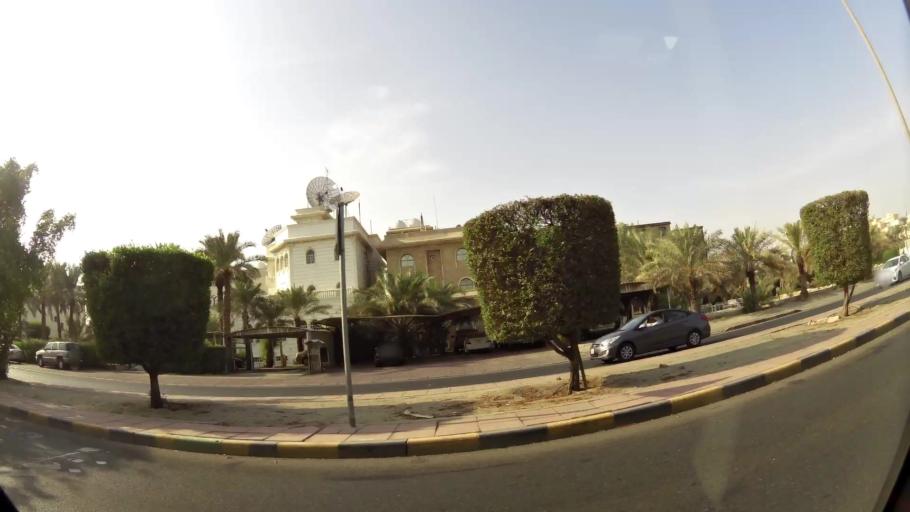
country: KW
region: Mubarak al Kabir
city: Mubarak al Kabir
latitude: 29.1725
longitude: 48.0763
